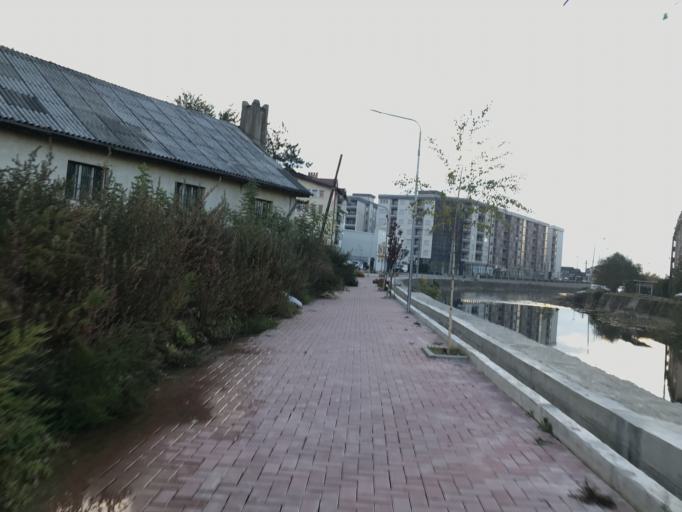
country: XK
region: Pec
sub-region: Komuna e Pejes
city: Peje
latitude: 42.6551
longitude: 20.2986
